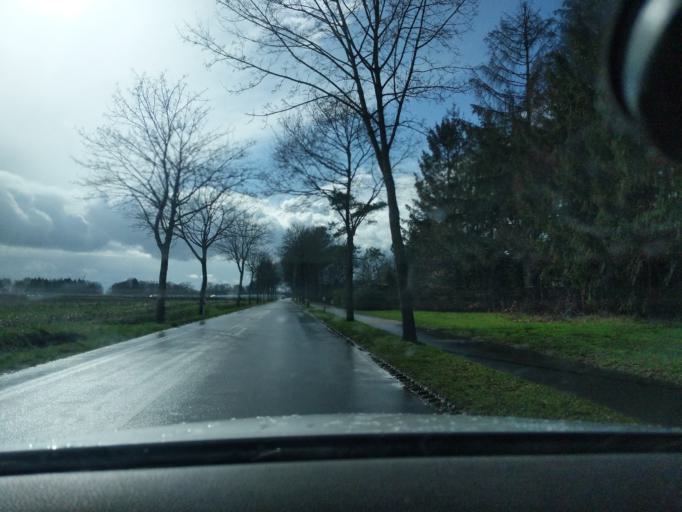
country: DE
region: Lower Saxony
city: Hechthausen
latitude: 53.6134
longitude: 9.2392
